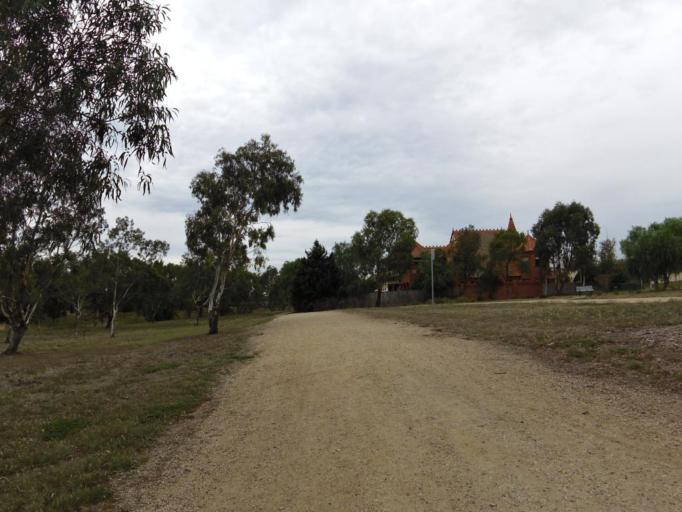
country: AU
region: Victoria
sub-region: Brimbank
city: Taylors Lakes
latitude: -37.7004
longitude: 144.7830
